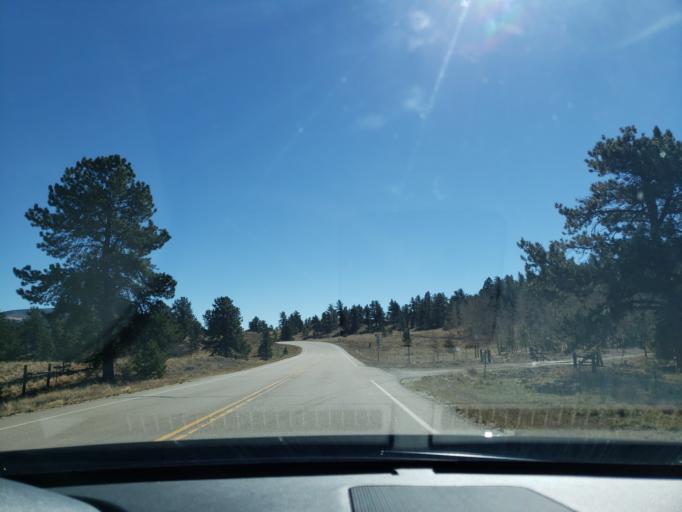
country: US
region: Colorado
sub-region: Chaffee County
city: Buena Vista
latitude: 38.8793
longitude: -105.6768
